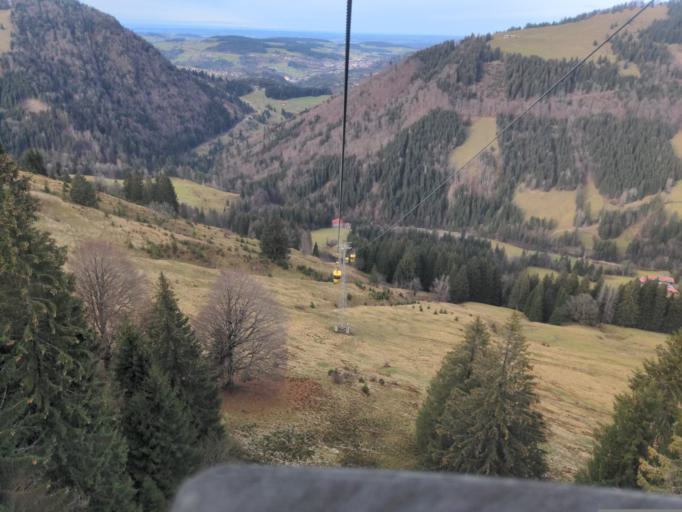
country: DE
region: Bavaria
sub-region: Swabia
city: Balderschwang
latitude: 47.5018
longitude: 10.0645
